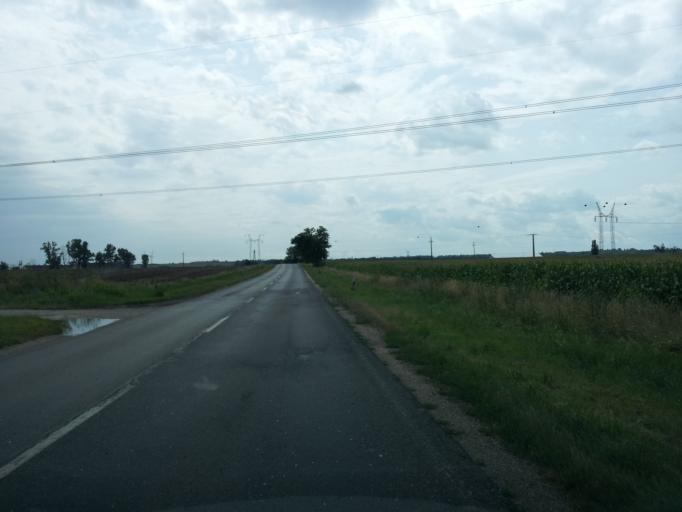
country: HU
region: Fejer
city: Lepseny
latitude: 46.9875
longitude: 18.2300
